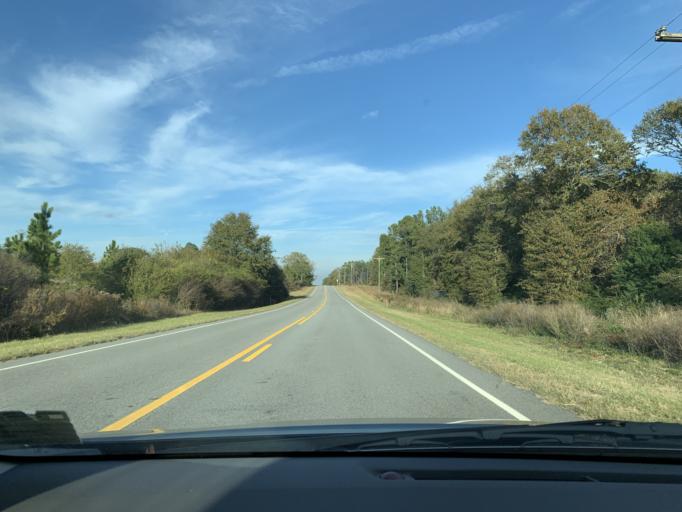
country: US
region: Georgia
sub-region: Irwin County
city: Ocilla
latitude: 31.6229
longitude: -83.4262
